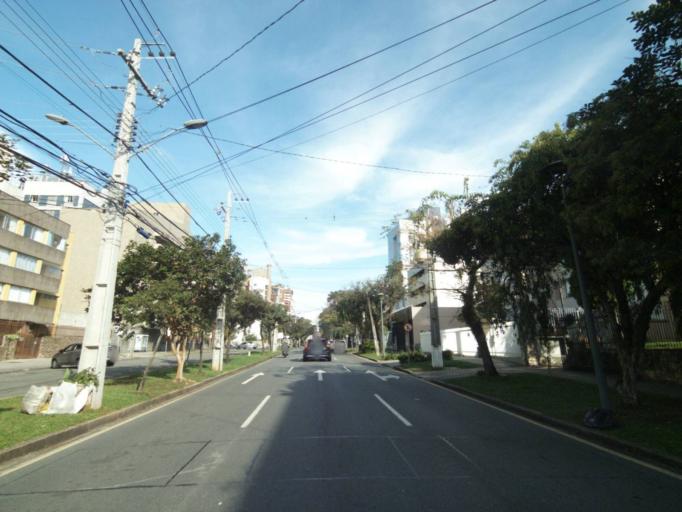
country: BR
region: Parana
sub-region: Curitiba
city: Curitiba
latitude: -25.4313
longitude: -49.2850
